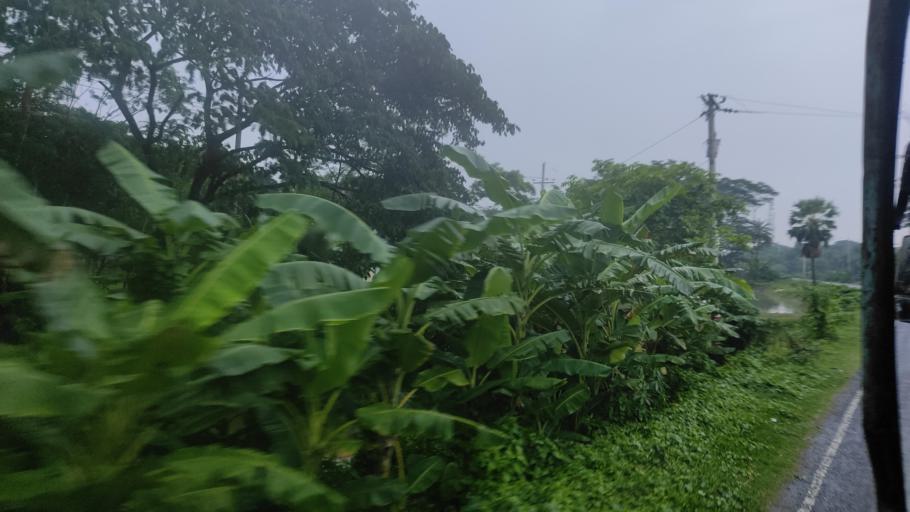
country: BD
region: Barisal
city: Bhandaria
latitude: 22.3012
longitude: 90.3243
